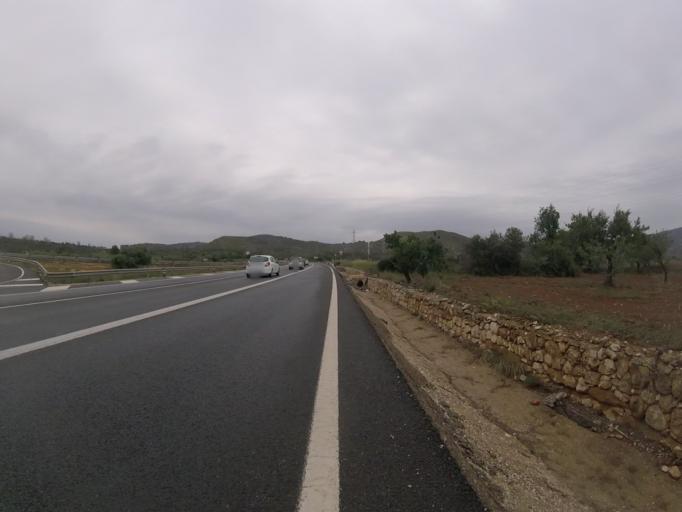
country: ES
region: Valencia
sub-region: Provincia de Castello
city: Alcala de Xivert
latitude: 40.2687
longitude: 0.2409
